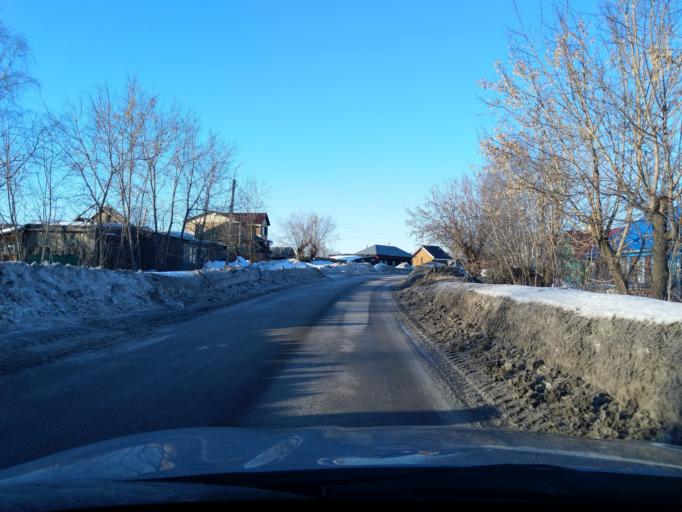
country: RU
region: Perm
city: Polazna
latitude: 58.2964
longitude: 56.4159
